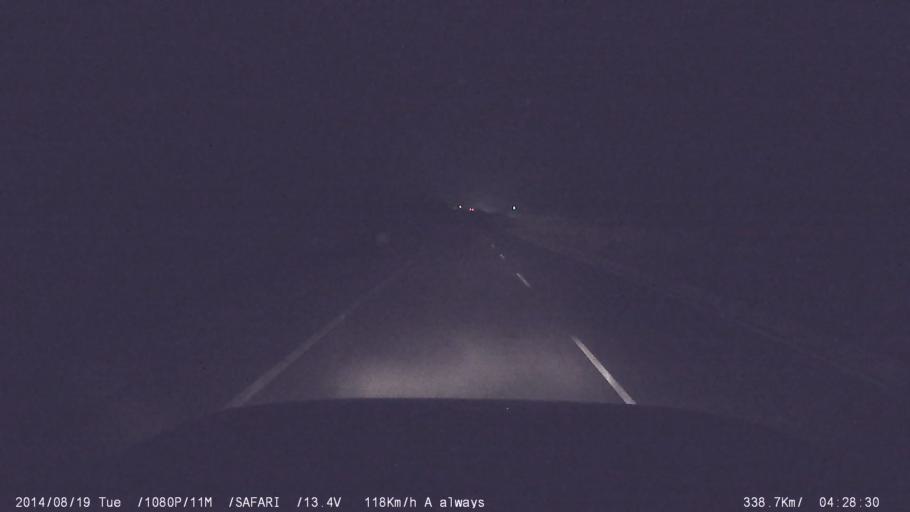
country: IN
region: Tamil Nadu
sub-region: Erode
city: Vijayapuri
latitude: 11.2474
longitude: 77.5254
